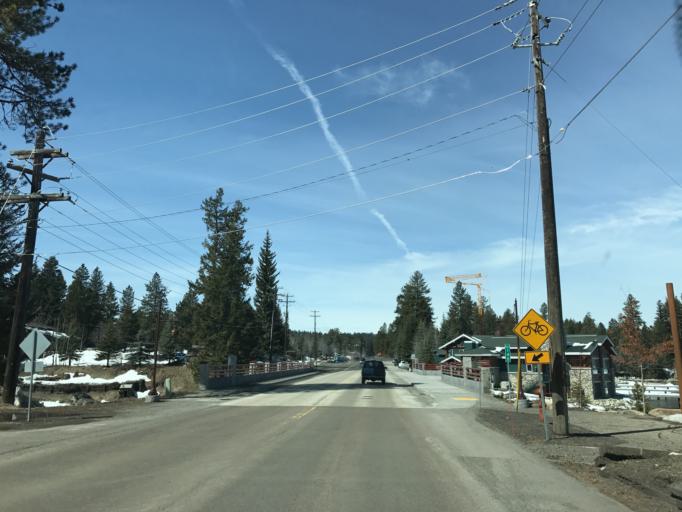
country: US
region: Idaho
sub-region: Valley County
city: McCall
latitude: 44.9118
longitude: -116.1181
